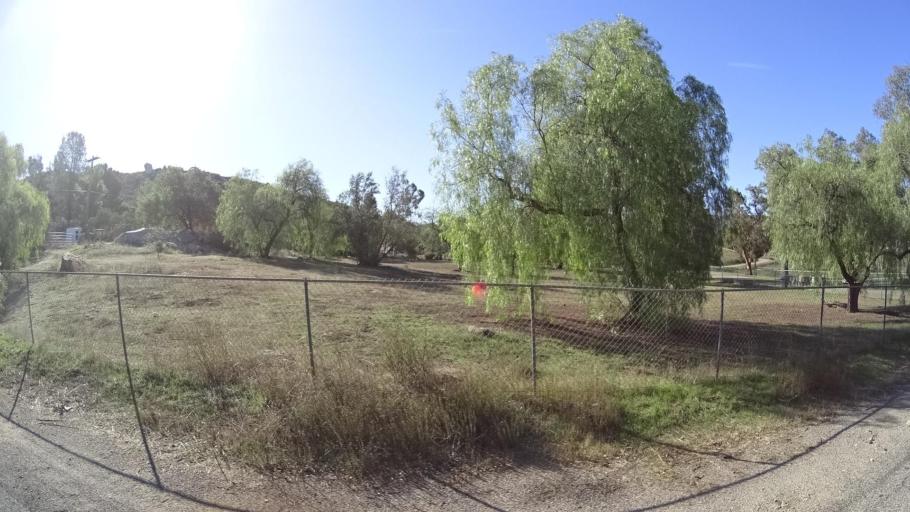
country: US
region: California
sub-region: San Diego County
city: Jamul
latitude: 32.6654
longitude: -116.7886
